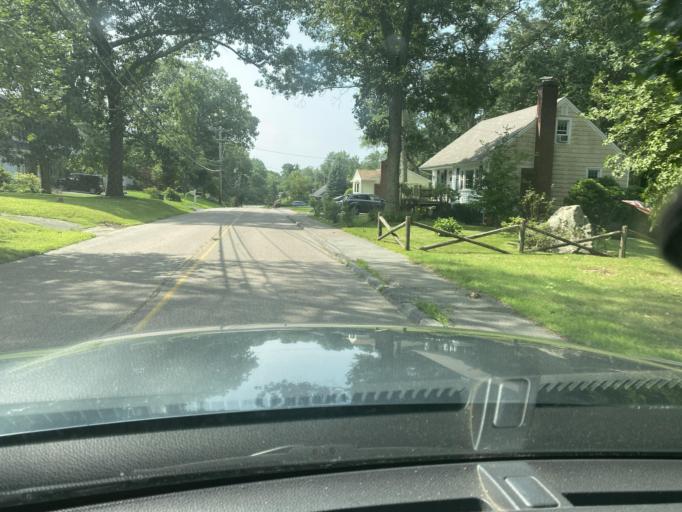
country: US
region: Massachusetts
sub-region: Norfolk County
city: Bellingham
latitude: 42.1161
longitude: -71.4749
